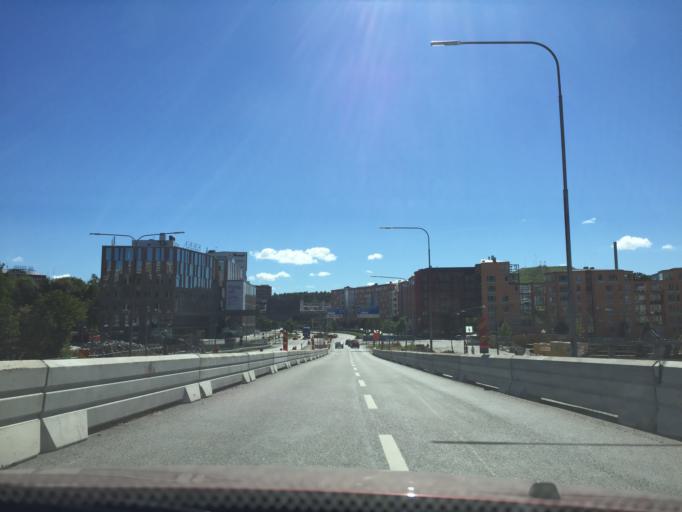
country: SE
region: Stockholm
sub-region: Stockholms Kommun
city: OEstermalm
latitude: 59.3074
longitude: 18.1130
